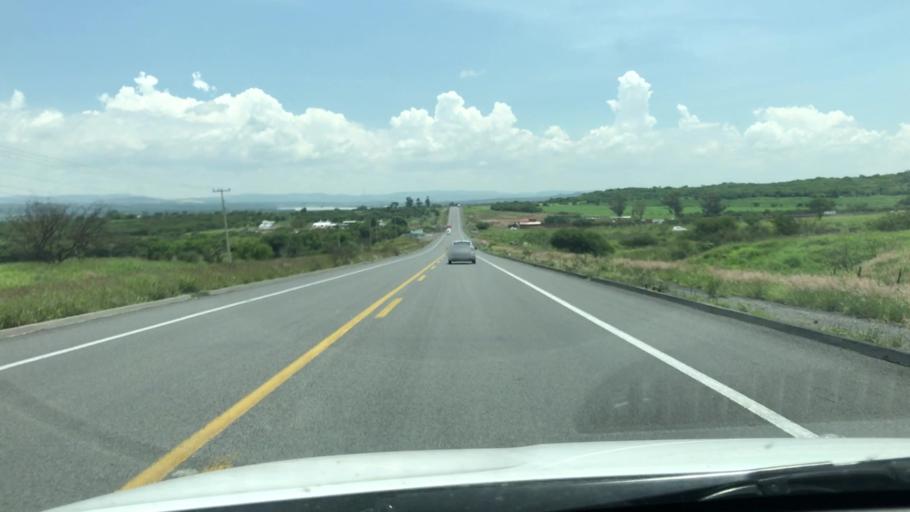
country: MX
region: Jalisco
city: Degollado
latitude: 20.3512
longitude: -102.1556
